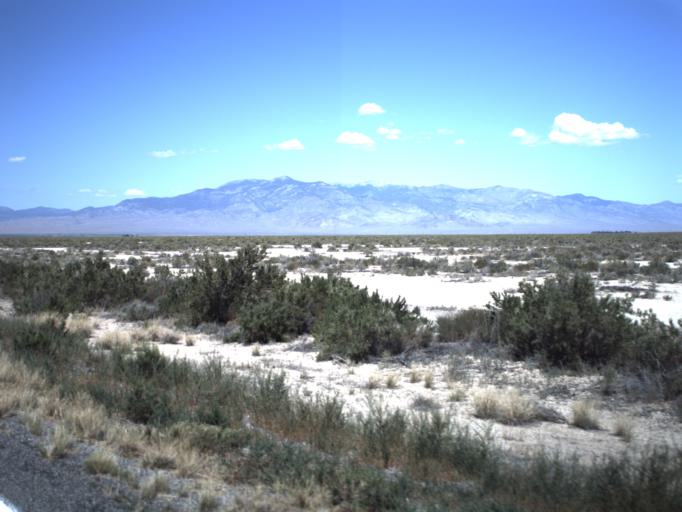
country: US
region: Nevada
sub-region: White Pine County
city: McGill
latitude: 39.0462
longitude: -113.9061
